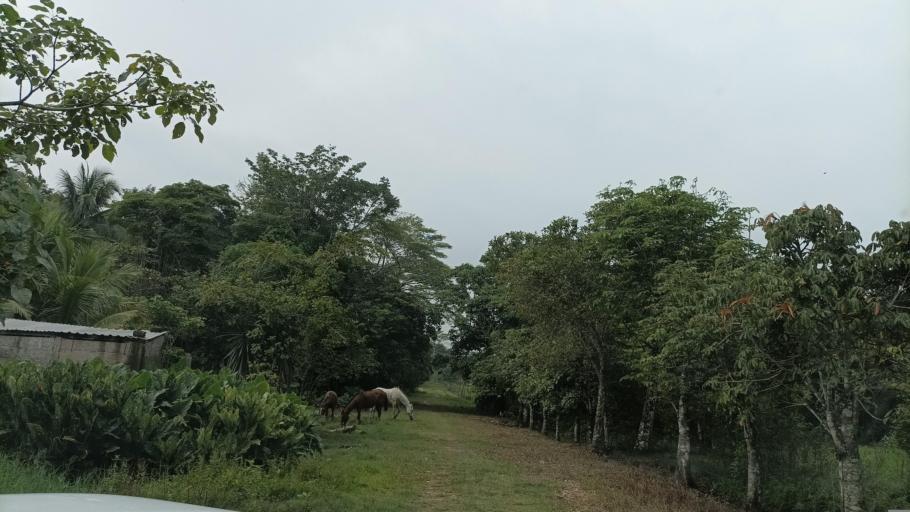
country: MX
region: Veracruz
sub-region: Uxpanapa
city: Poblado 10
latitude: 17.5429
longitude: -94.2380
